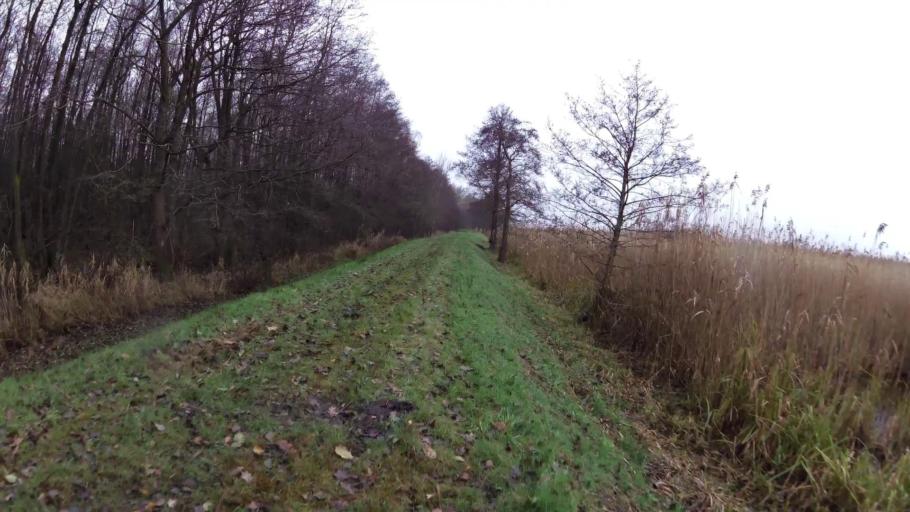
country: PL
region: West Pomeranian Voivodeship
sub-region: Powiat koszalinski
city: Mielno
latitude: 54.2530
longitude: 16.1232
